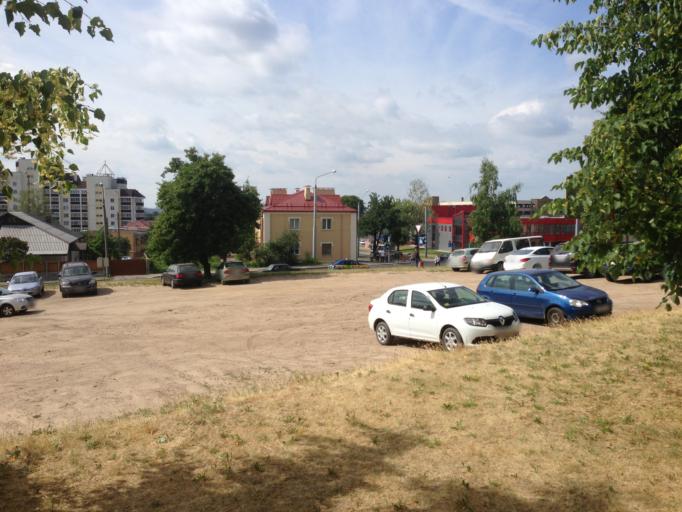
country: BY
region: Grodnenskaya
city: Hrodna
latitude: 53.6960
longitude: 23.8405
